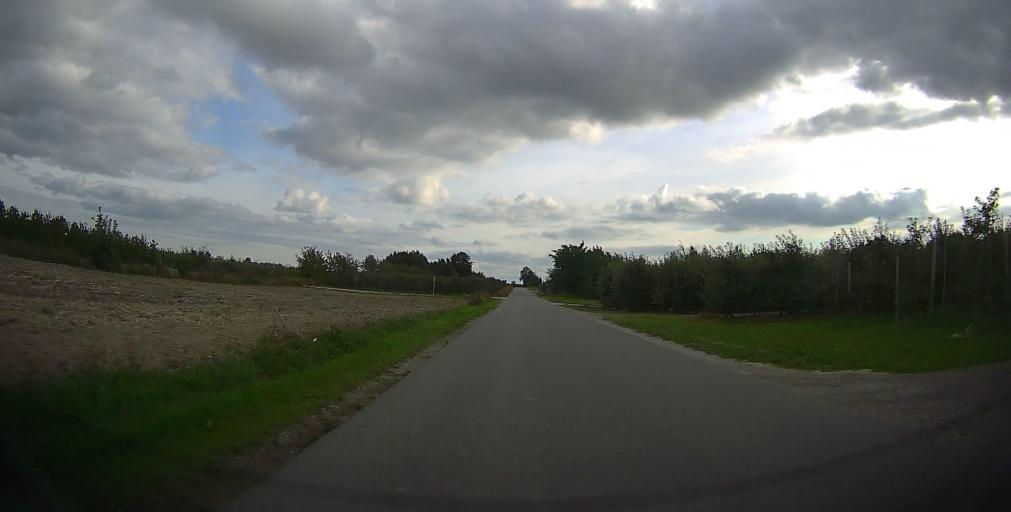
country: PL
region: Masovian Voivodeship
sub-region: Powiat bialobrzeski
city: Promna
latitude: 51.7203
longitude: 20.9586
